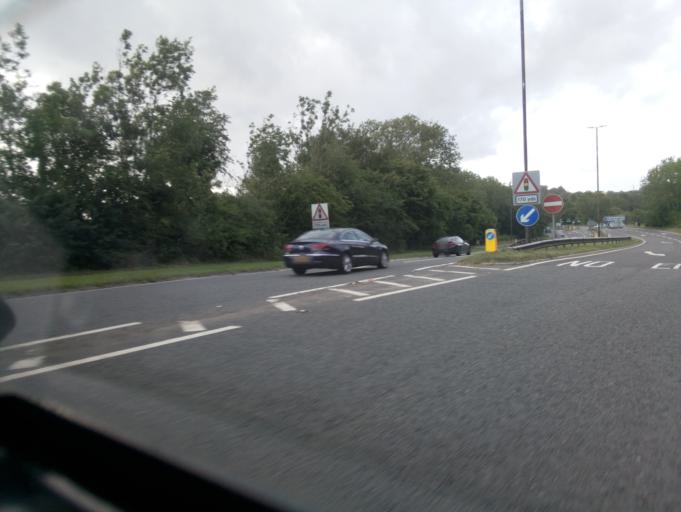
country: GB
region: England
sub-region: Gloucestershire
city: Shipton Village
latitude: 51.8743
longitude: -1.9643
